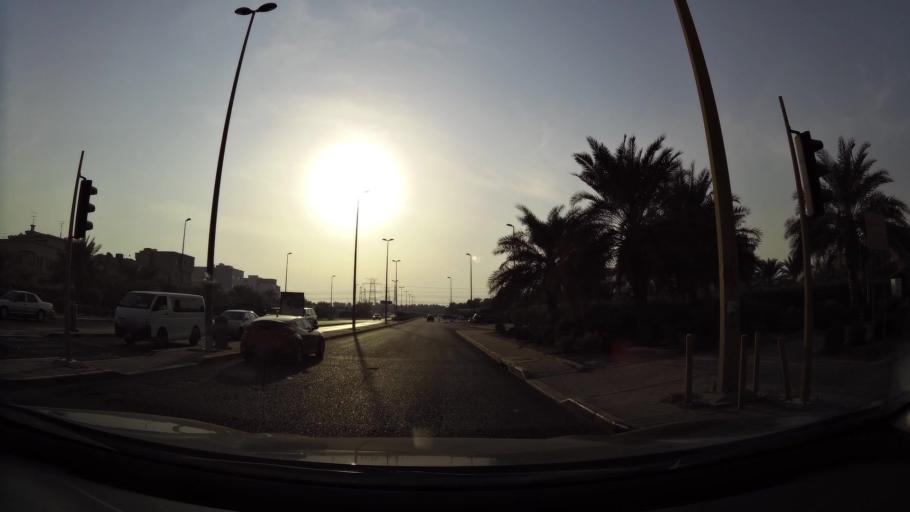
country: KW
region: Mubarak al Kabir
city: Sabah as Salim
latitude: 29.2211
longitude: 48.0613
